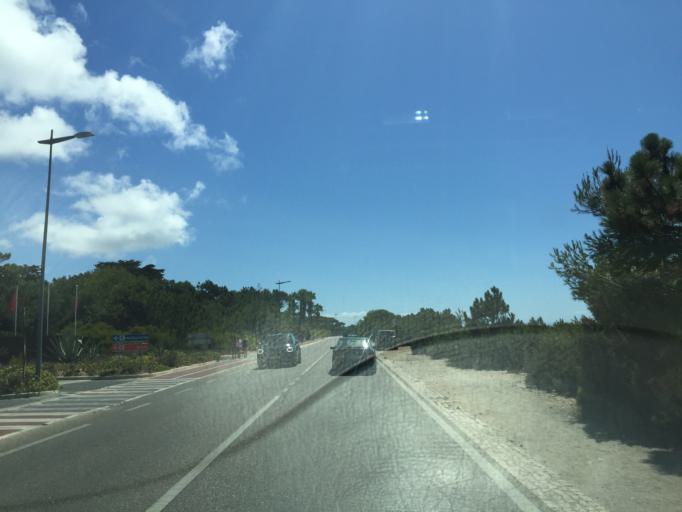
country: PT
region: Lisbon
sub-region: Cascais
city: Cascais
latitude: 38.6977
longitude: -9.4638
